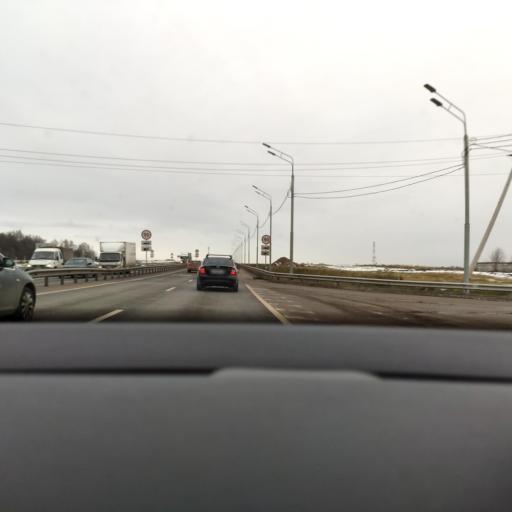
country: RU
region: Moskovskaya
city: Zvenigorod
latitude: 55.6879
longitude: 36.8873
